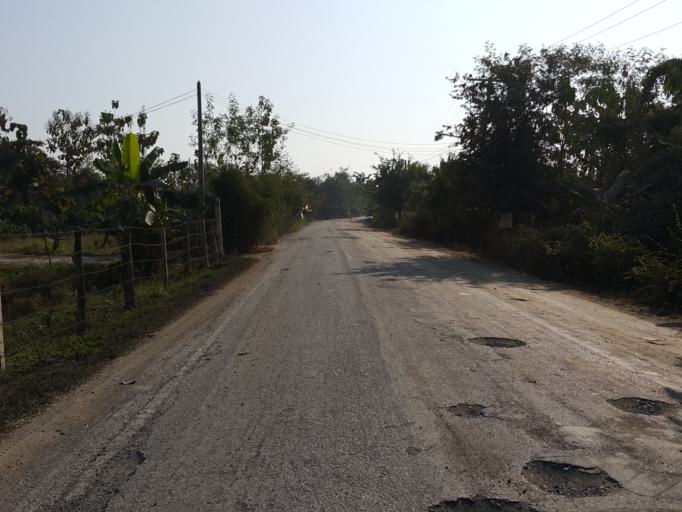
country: TH
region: Chiang Mai
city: San Kamphaeng
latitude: 18.6971
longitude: 99.1102
